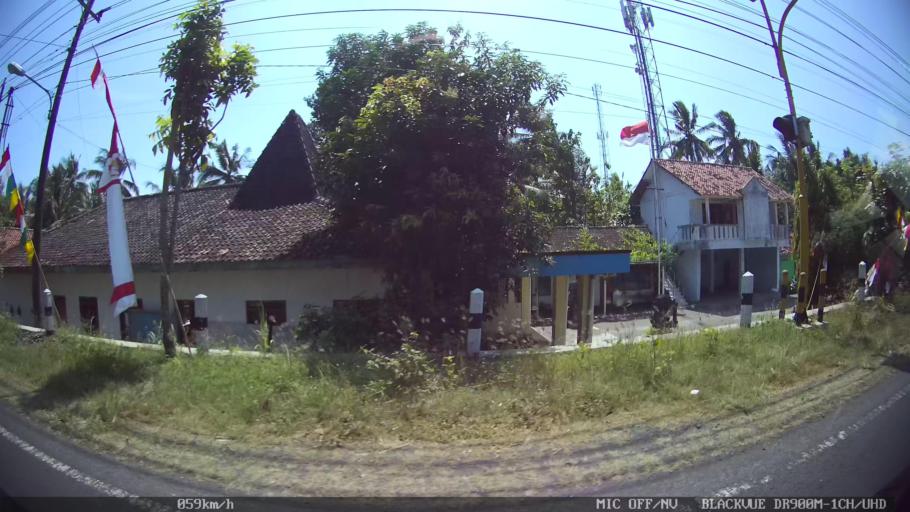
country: ID
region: Daerah Istimewa Yogyakarta
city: Srandakan
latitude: -7.9132
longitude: 110.0941
